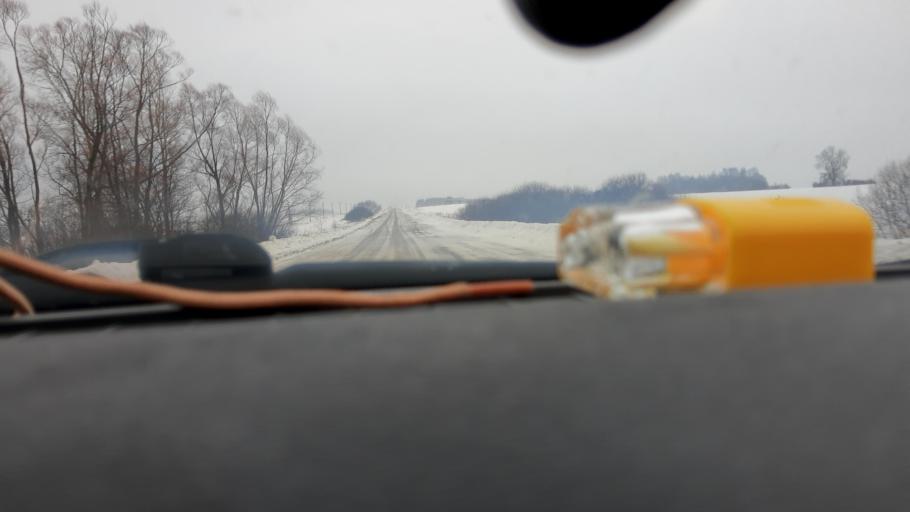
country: RU
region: Bashkortostan
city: Iglino
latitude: 54.6251
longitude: 56.4258
